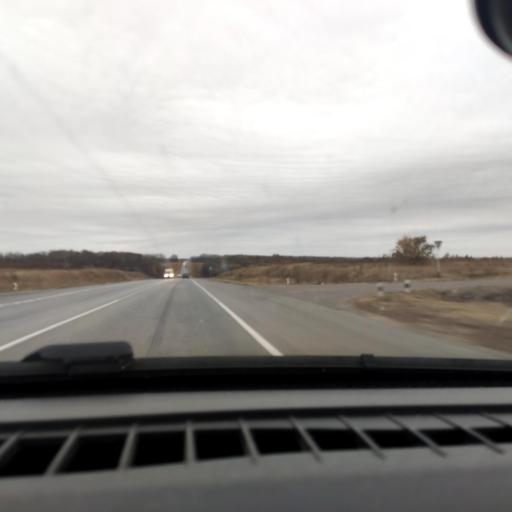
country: RU
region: Voronezj
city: Strelitsa
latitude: 51.5244
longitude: 38.9685
